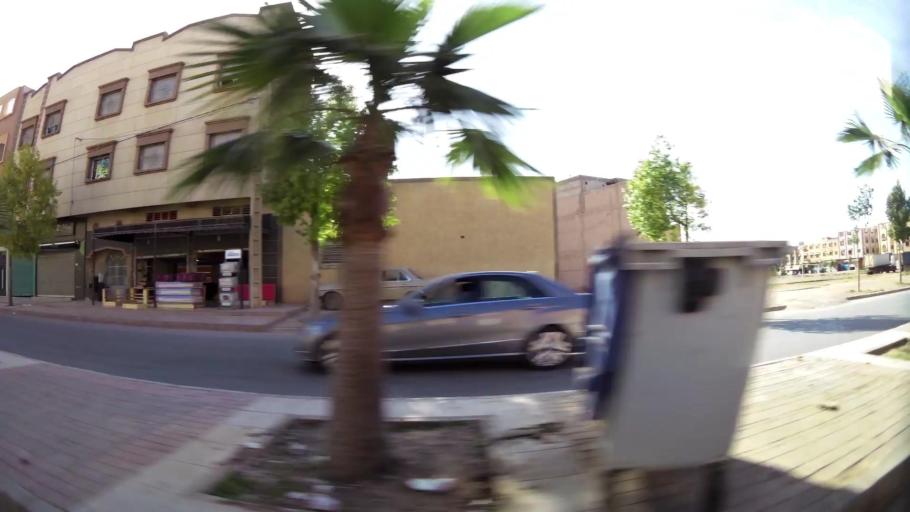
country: MA
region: Oriental
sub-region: Oujda-Angad
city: Oujda
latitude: 34.6728
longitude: -1.8932
